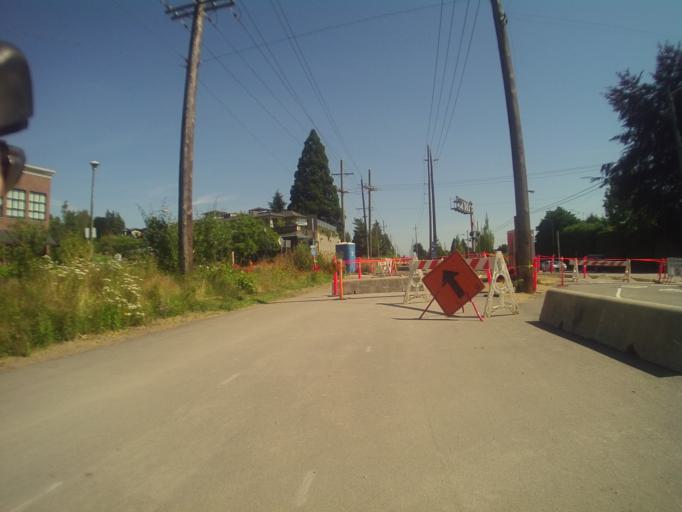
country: CA
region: British Columbia
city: Vancouver
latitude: 49.2198
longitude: -123.1505
